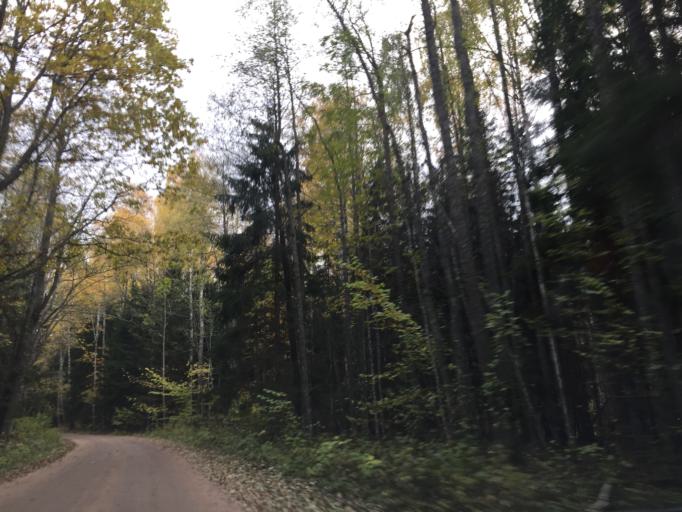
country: LV
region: Salacgrivas
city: Salacgriva
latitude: 57.5766
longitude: 24.3843
